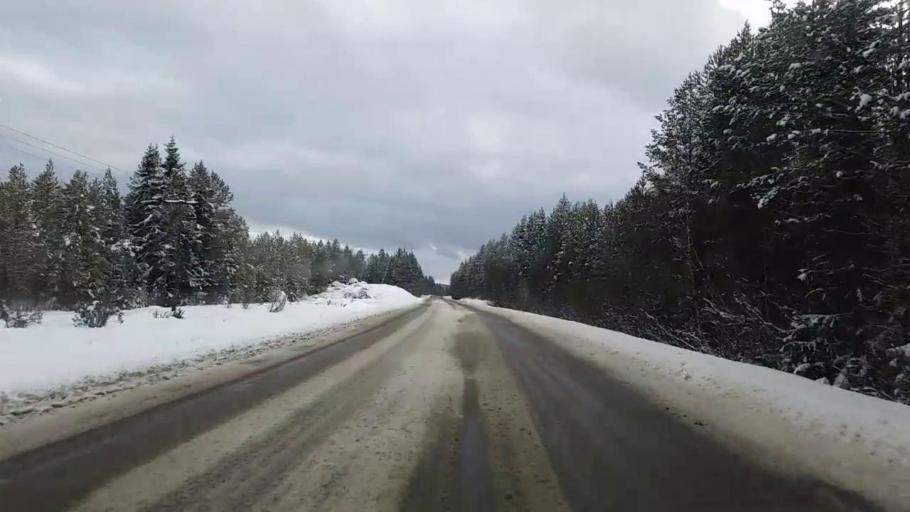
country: SE
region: Vaesternorrland
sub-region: Ange Kommun
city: Ange
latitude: 62.0839
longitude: 15.0955
